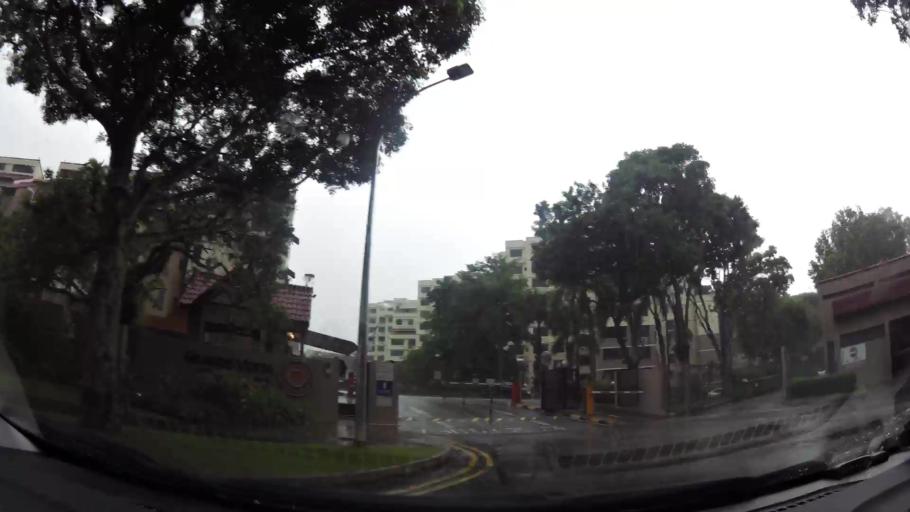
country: MY
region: Johor
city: Kampung Pasir Gudang Baru
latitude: 1.3892
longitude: 103.8518
